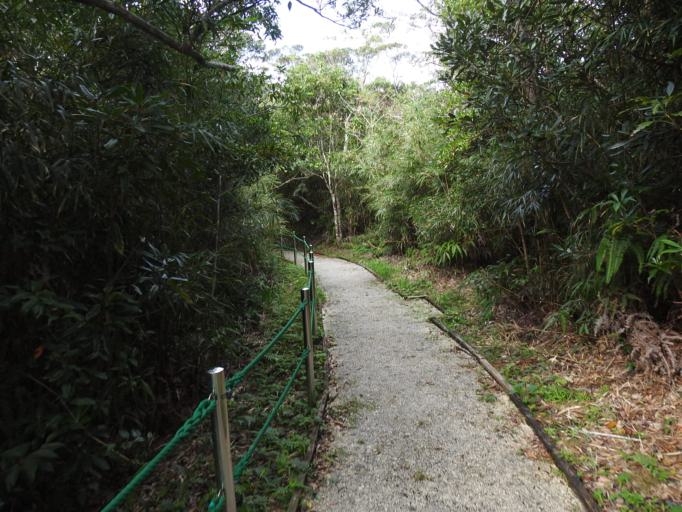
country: JP
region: Okinawa
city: Nago
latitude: 26.7214
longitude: 128.2654
